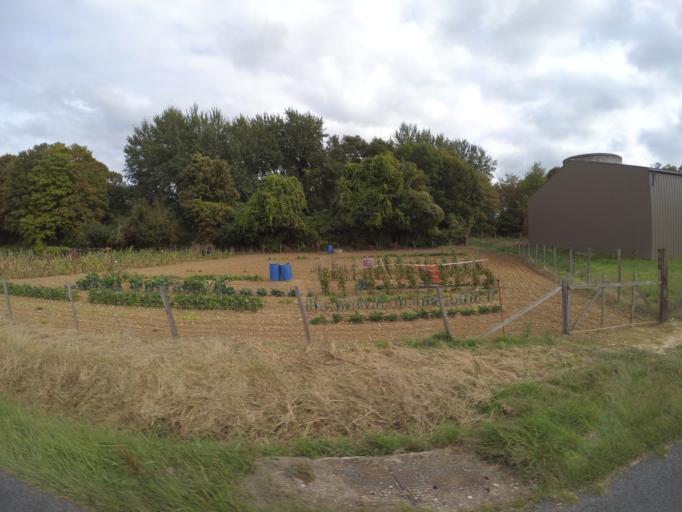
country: FR
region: Centre
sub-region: Departement d'Indre-et-Loire
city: Reugny
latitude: 47.4578
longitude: 0.8777
